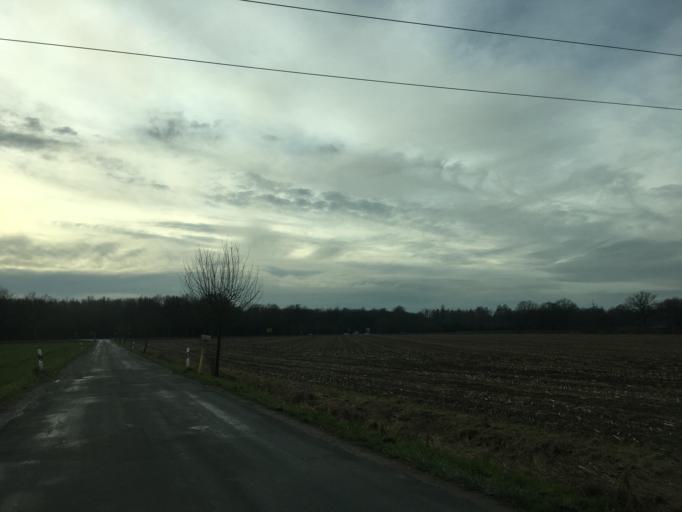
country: DE
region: North Rhine-Westphalia
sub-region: Regierungsbezirk Munster
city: Dulmen
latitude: 51.8380
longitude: 7.3249
